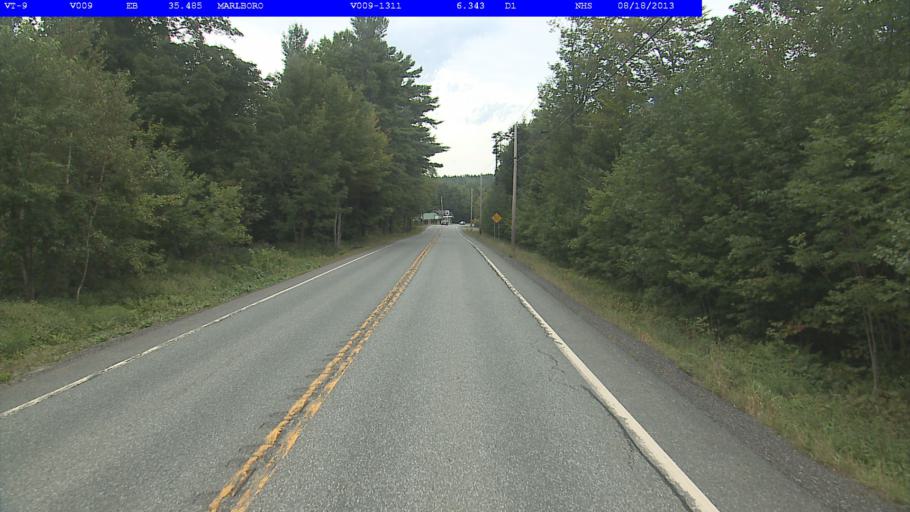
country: US
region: Vermont
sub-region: Windham County
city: West Brattleboro
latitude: 42.8760
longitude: -72.7104
